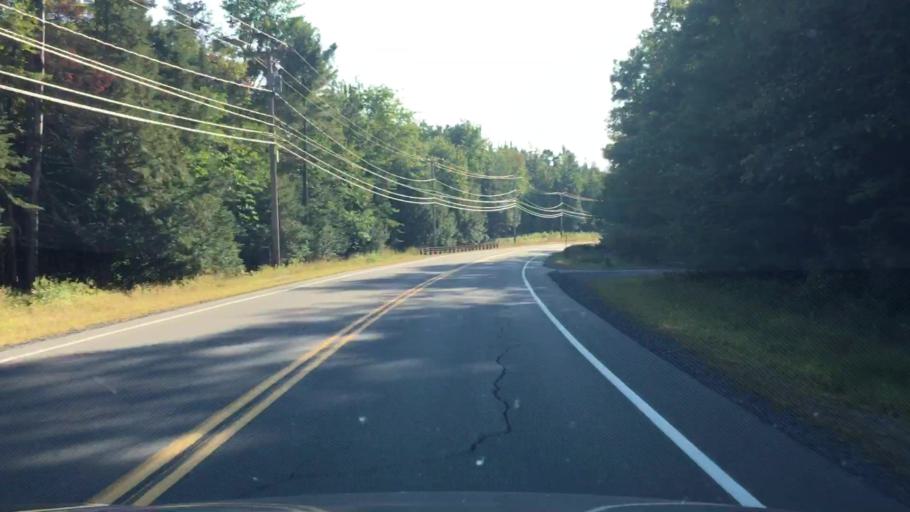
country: US
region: New Hampshire
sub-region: Grafton County
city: Littleton
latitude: 44.3109
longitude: -71.8370
